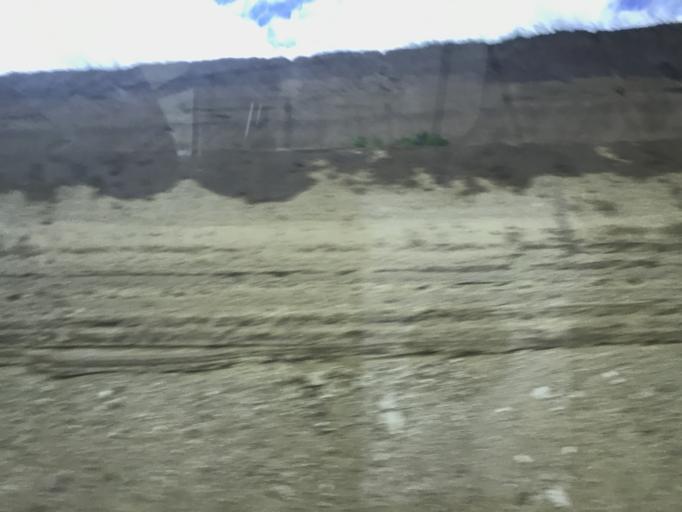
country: GT
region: Chimaltenango
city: El Tejar
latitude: 14.6350
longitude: -90.7928
